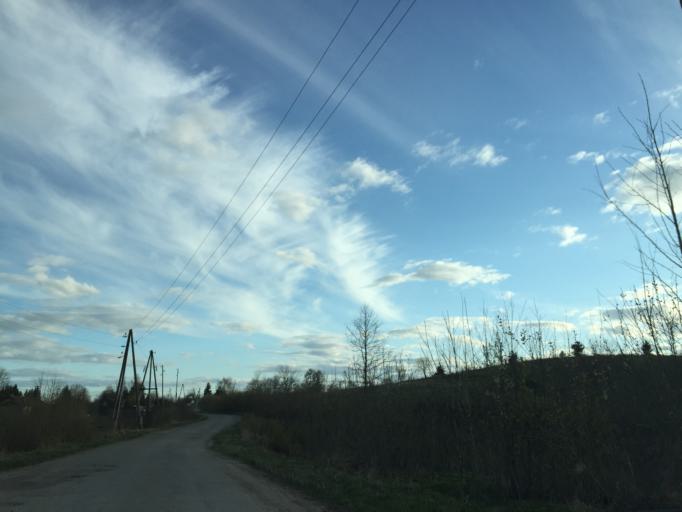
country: LV
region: Rezekne
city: Rezekne
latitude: 56.5833
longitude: 27.3377
